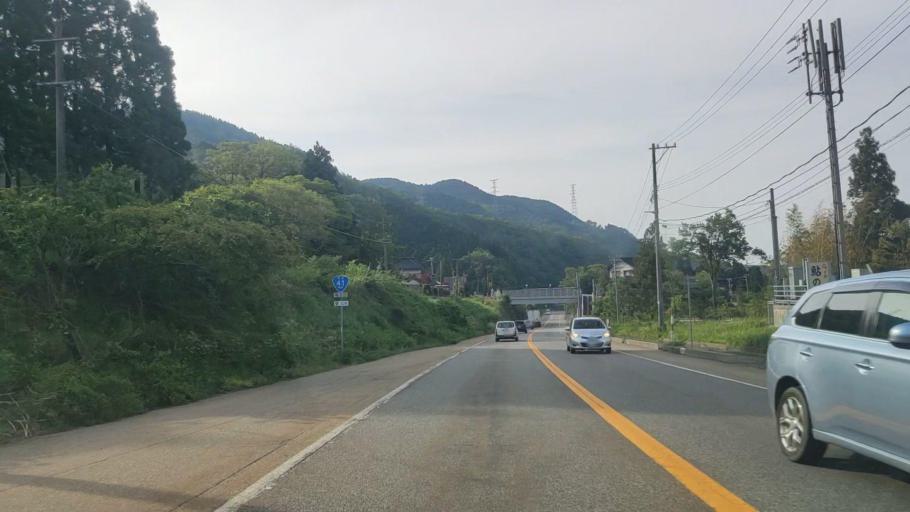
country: JP
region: Toyama
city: Yatsuomachi-higashikumisaka
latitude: 36.5068
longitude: 137.2300
